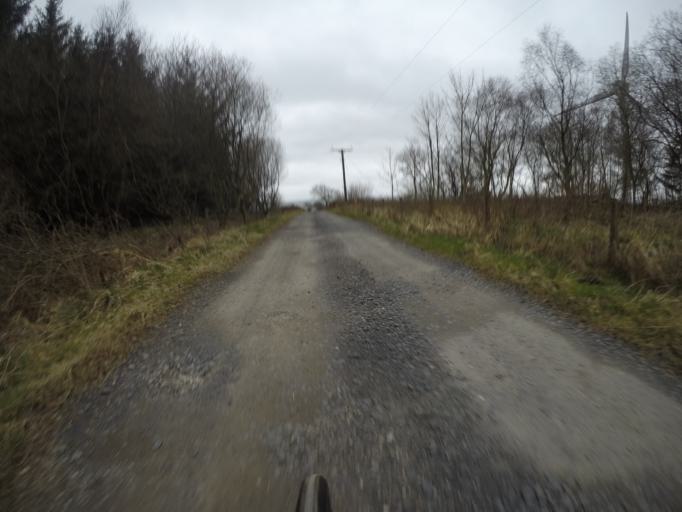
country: GB
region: Scotland
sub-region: East Ayrshire
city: Newmilns
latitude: 55.6273
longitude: -4.3426
